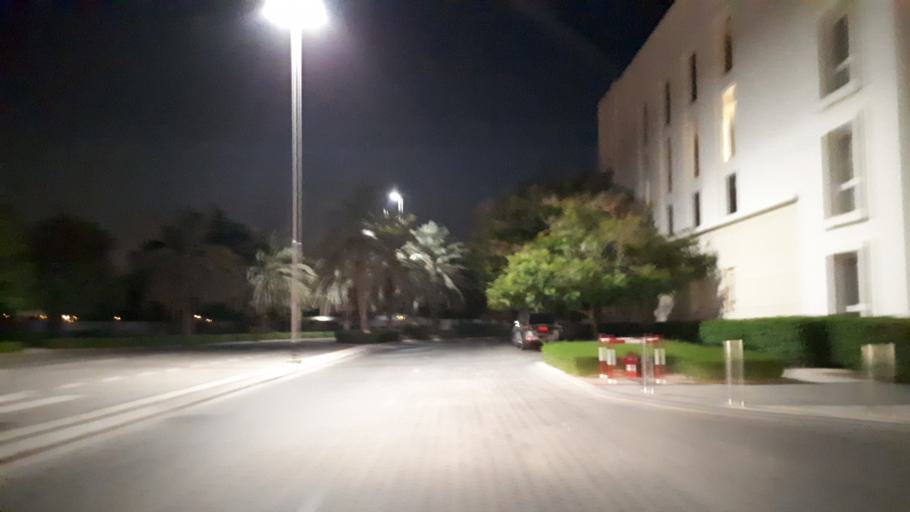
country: OM
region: Muhafazat Masqat
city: As Sib al Jadidah
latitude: 23.6285
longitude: 58.2658
